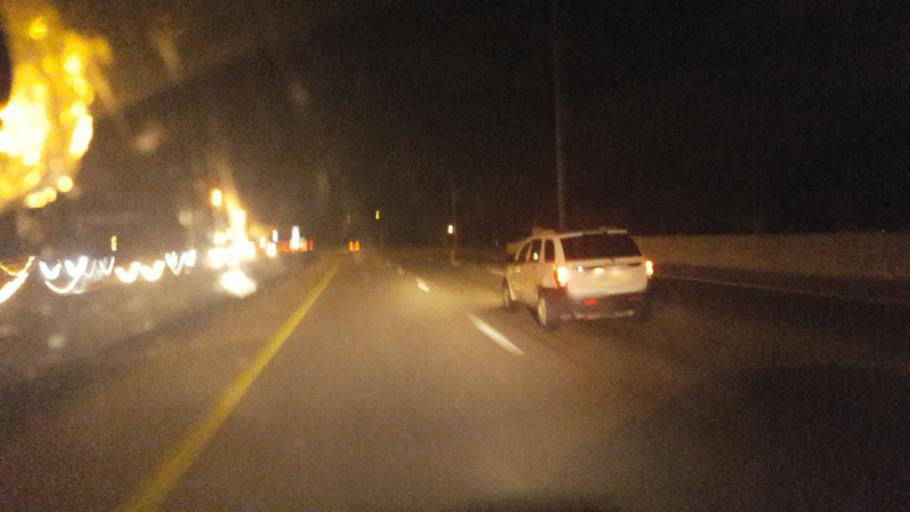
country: US
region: Indiana
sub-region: Marion County
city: Speedway
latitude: 39.7428
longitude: -86.2385
